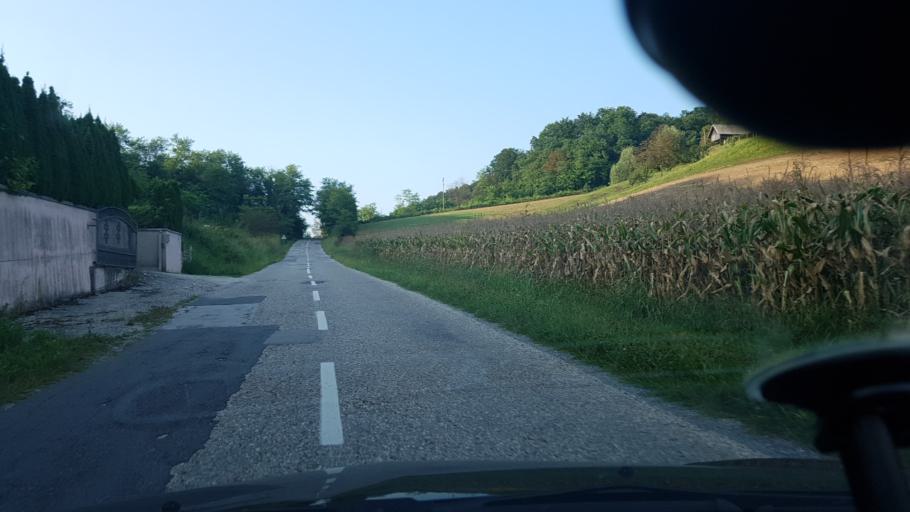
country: HR
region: Krapinsko-Zagorska
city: Zabok
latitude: 46.0396
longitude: 15.8594
